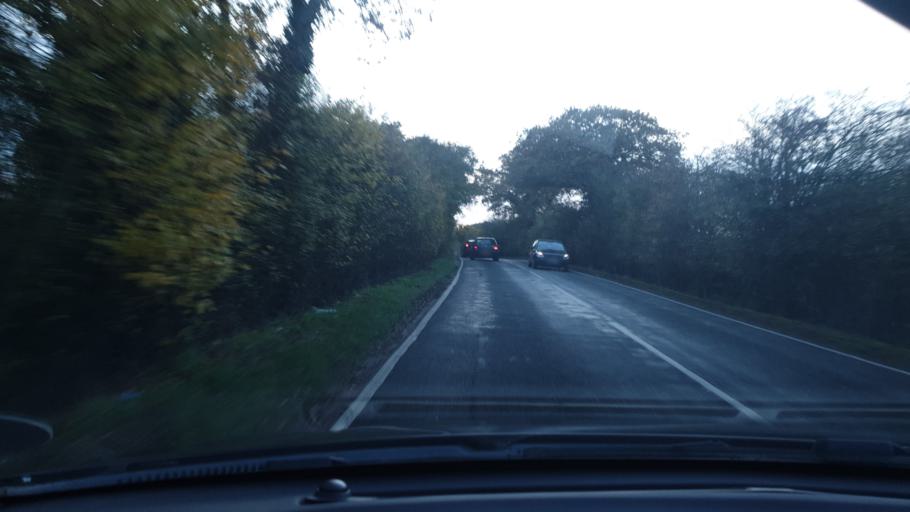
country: GB
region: England
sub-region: Essex
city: Dovercourt
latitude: 51.9086
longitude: 1.2131
